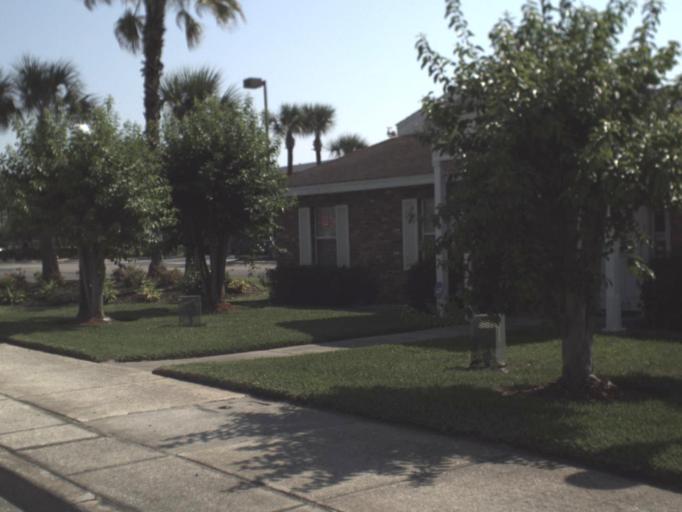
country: US
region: Florida
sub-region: Duval County
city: Jacksonville
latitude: 30.3101
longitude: -81.7519
